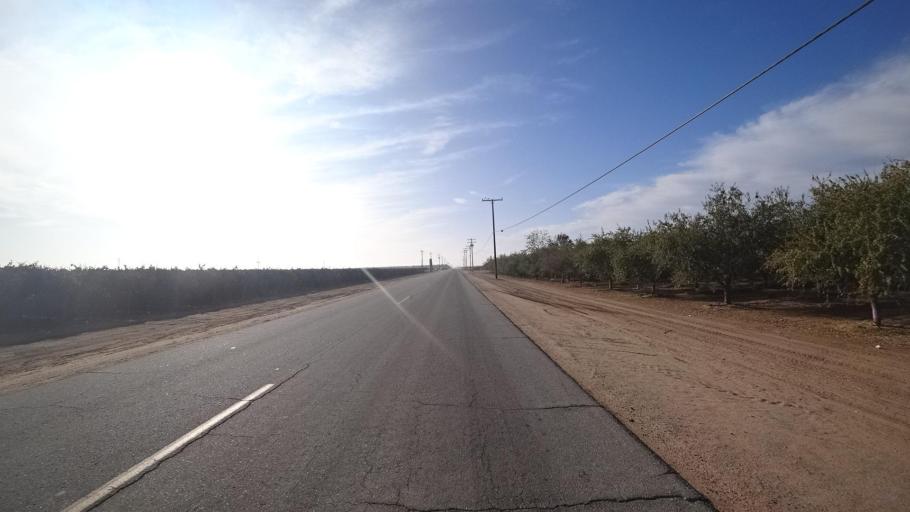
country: US
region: California
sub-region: Kern County
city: McFarland
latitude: 35.6622
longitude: -119.2047
